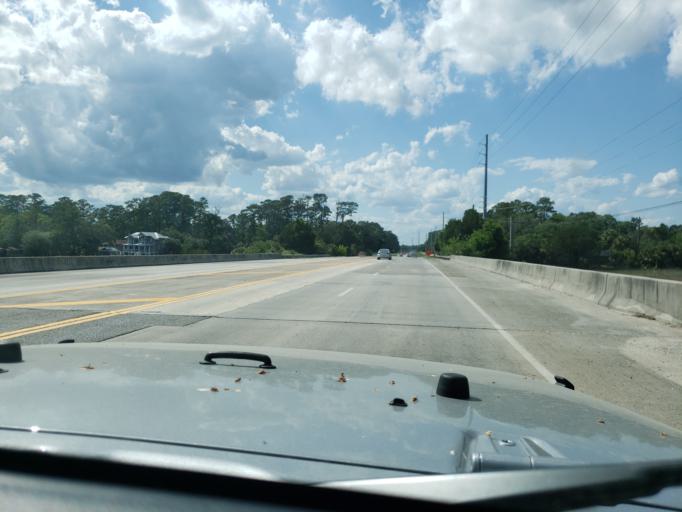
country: US
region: Georgia
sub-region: Chatham County
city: Whitemarsh Island
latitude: 32.0509
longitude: -81.0121
